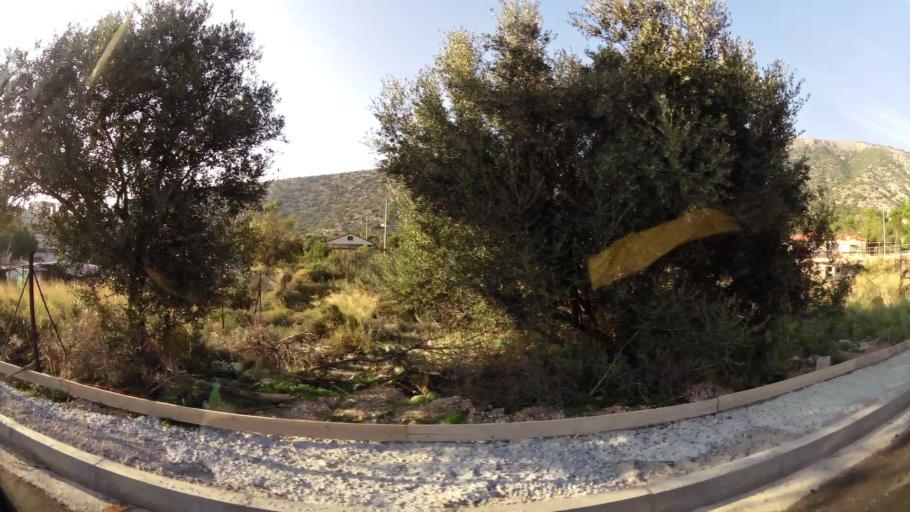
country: GR
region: Attica
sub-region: Nomarchia Athinas
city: Argyroupoli
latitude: 37.9019
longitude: 23.7749
